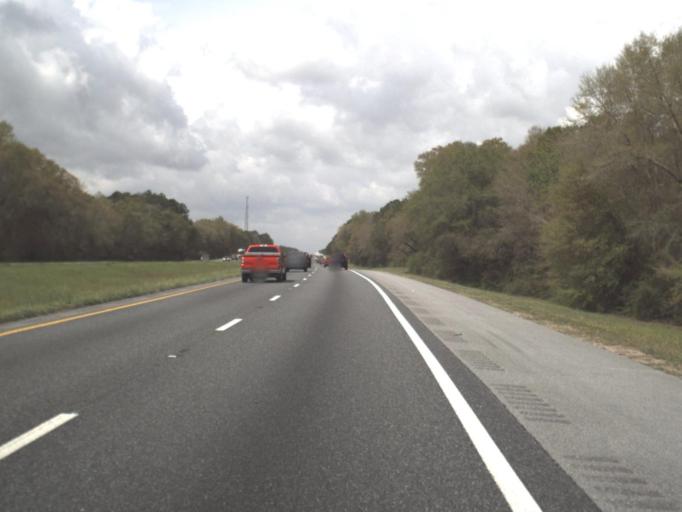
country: US
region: Florida
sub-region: Okaloosa County
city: Crestview
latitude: 30.7169
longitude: -86.6577
